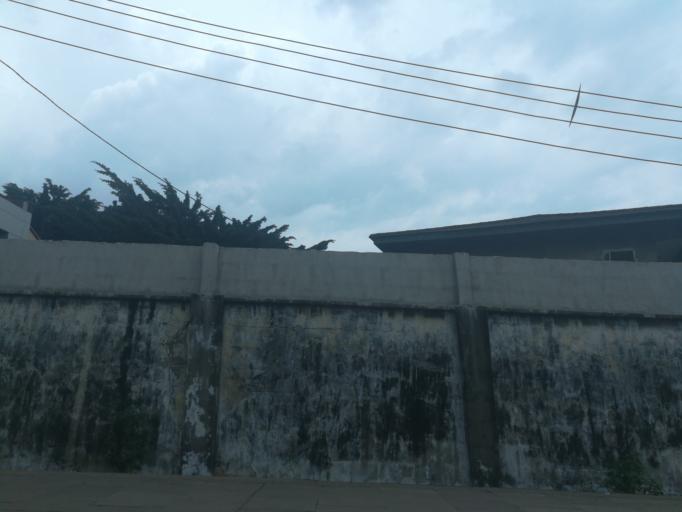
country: NG
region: Lagos
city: Lagos
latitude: 6.4439
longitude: 3.4007
